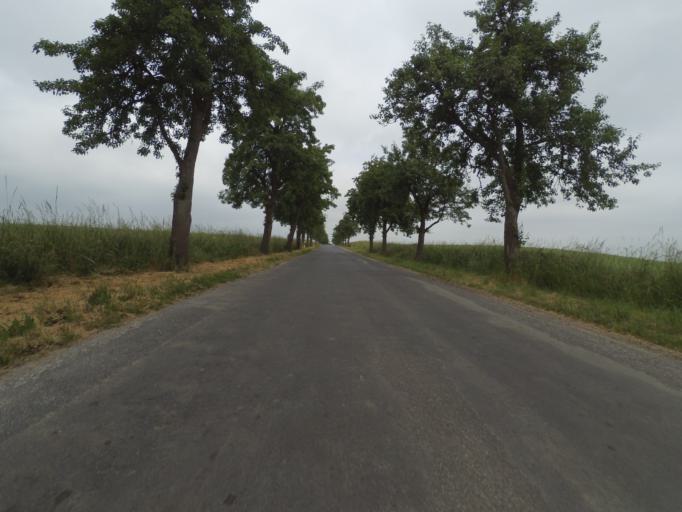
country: DE
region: Mecklenburg-Vorpommern
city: Goldberg
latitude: 53.5100
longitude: 12.1211
